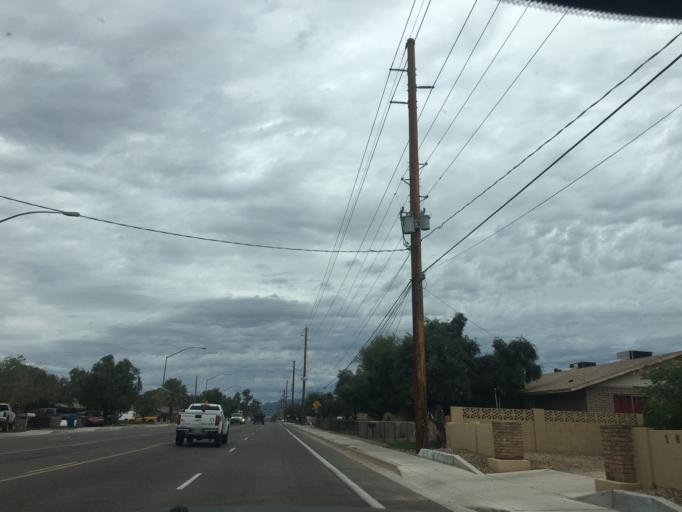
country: US
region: Arizona
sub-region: Maricopa County
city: Mesa
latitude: 33.4483
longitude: -111.8311
